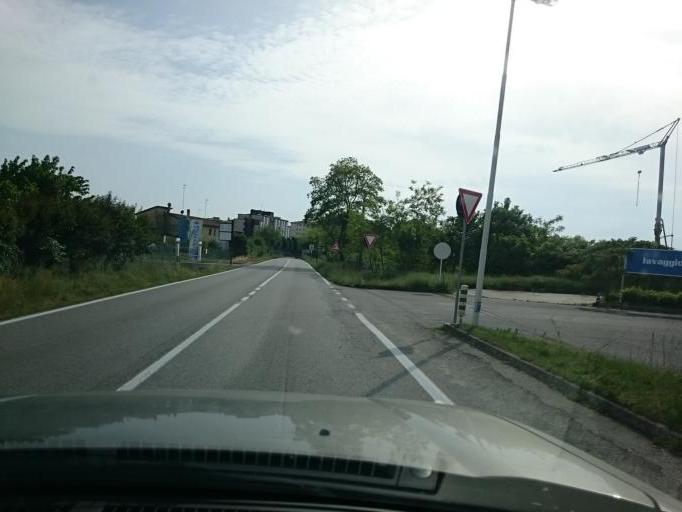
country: IT
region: Veneto
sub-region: Provincia di Venezia
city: Campalto
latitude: 45.4893
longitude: 12.3019
